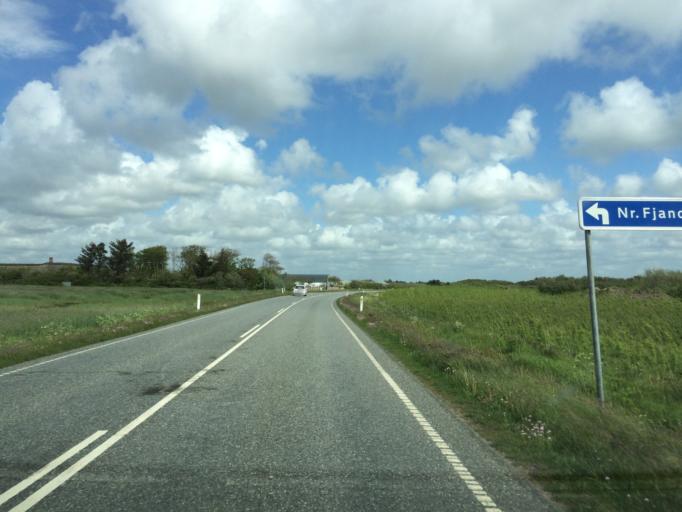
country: DK
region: Central Jutland
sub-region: Holstebro Kommune
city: Ulfborg
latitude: 56.3184
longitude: 8.1551
